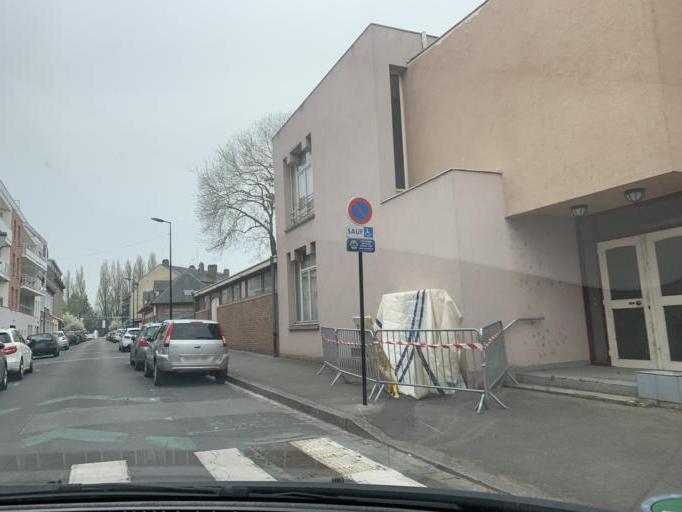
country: FR
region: Picardie
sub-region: Departement de la Somme
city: Abbeville
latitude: 50.1056
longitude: 1.8296
